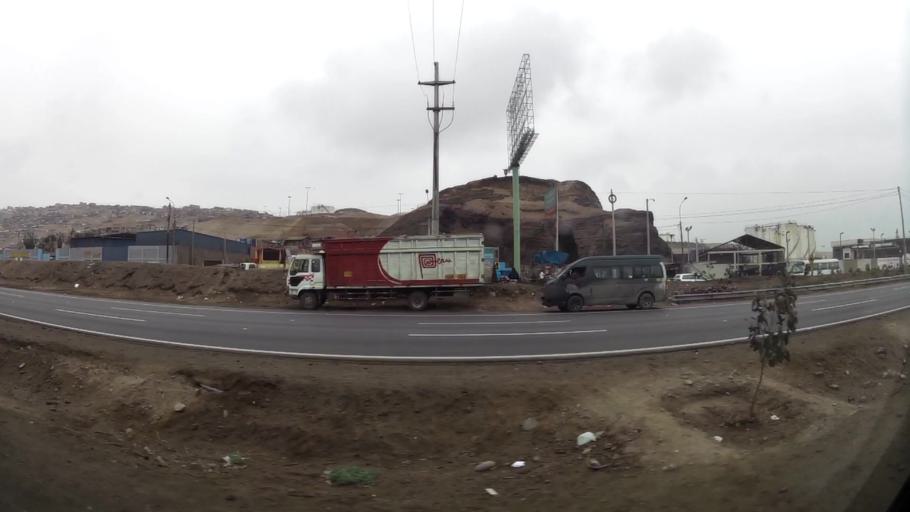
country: PE
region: Lima
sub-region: Lima
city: Punta Hermosa
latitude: -12.2530
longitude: -76.9272
